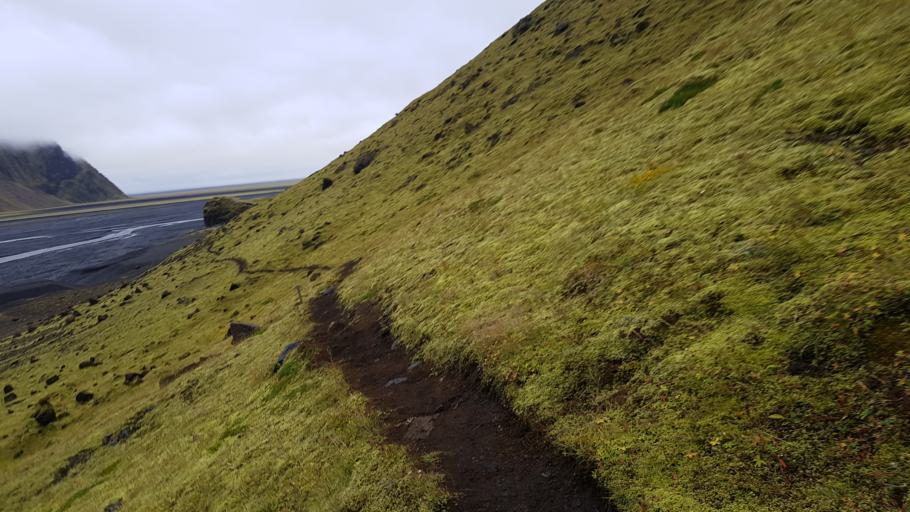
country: IS
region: South
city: Vestmannaeyjar
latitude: 63.5309
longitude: -18.8504
